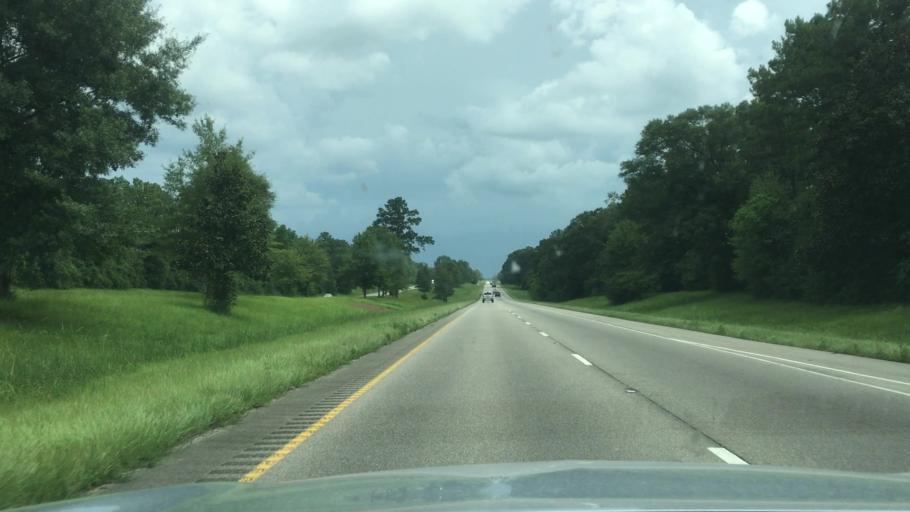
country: US
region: Mississippi
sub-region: Pearl River County
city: Carriere
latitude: 30.5678
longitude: -89.6360
